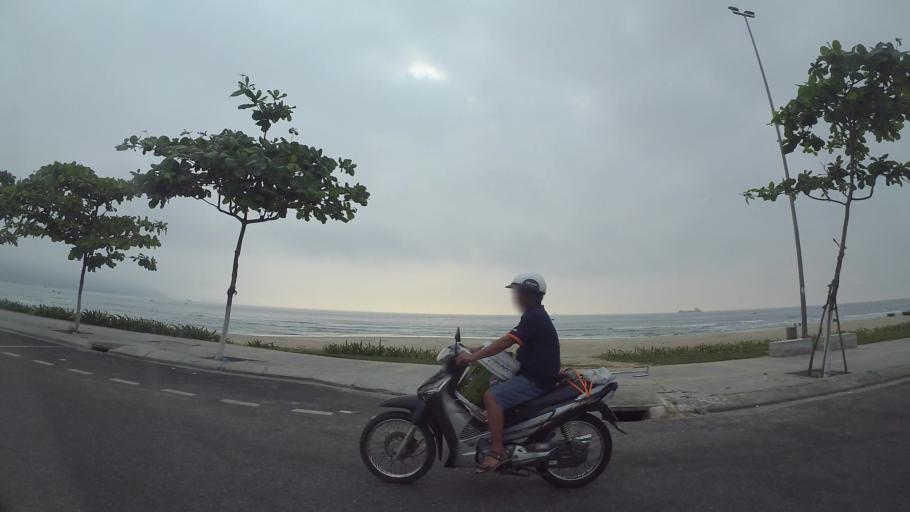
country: VN
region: Da Nang
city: Son Tra
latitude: 16.0826
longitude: 108.2477
